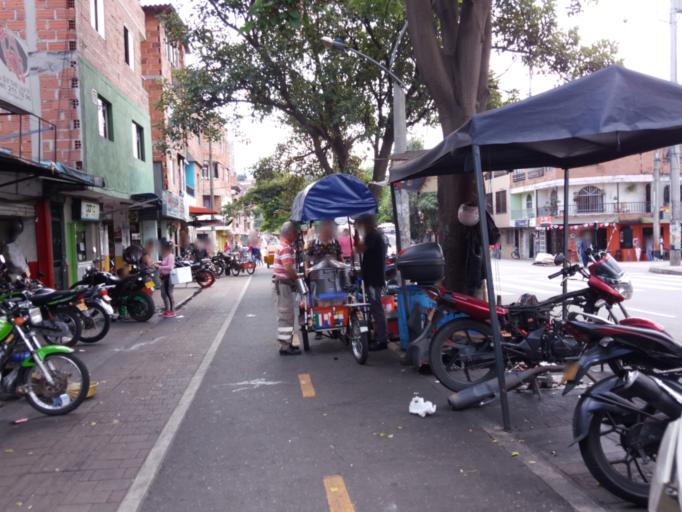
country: CO
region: Antioquia
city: Medellin
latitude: 6.2744
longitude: -75.5647
